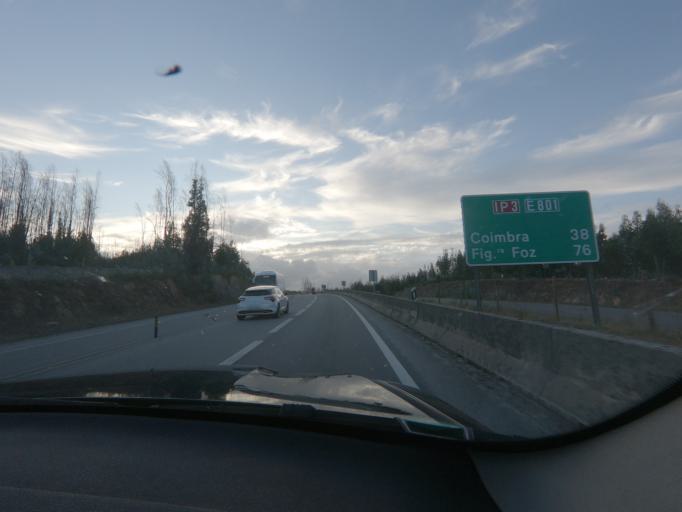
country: PT
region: Viseu
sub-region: Mortagua
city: Mortagua
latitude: 40.3517
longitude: -8.1901
